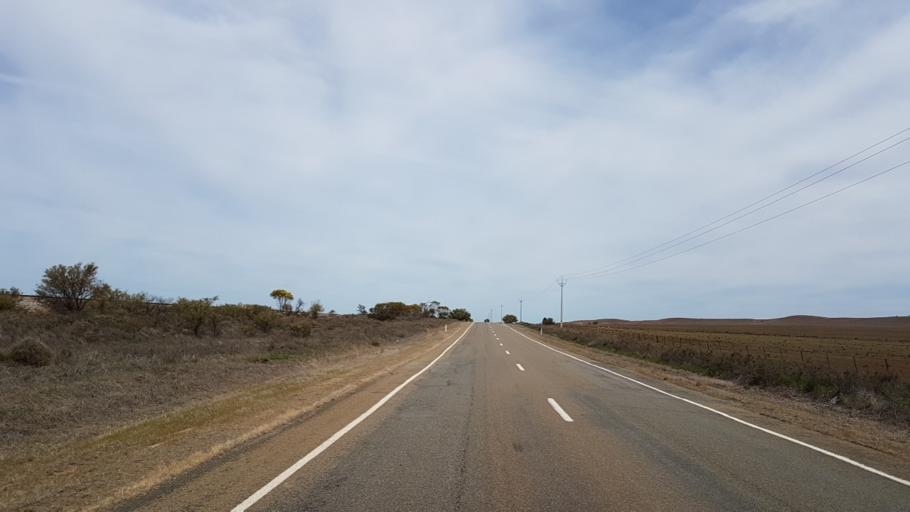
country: AU
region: South Australia
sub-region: Peterborough
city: Peterborough
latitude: -33.0124
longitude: 138.7628
